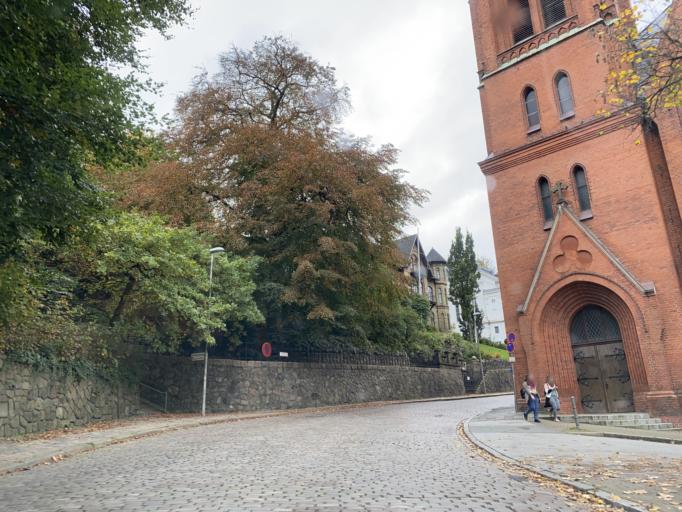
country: DE
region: Schleswig-Holstein
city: Flensburg
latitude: 54.7872
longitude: 9.4315
